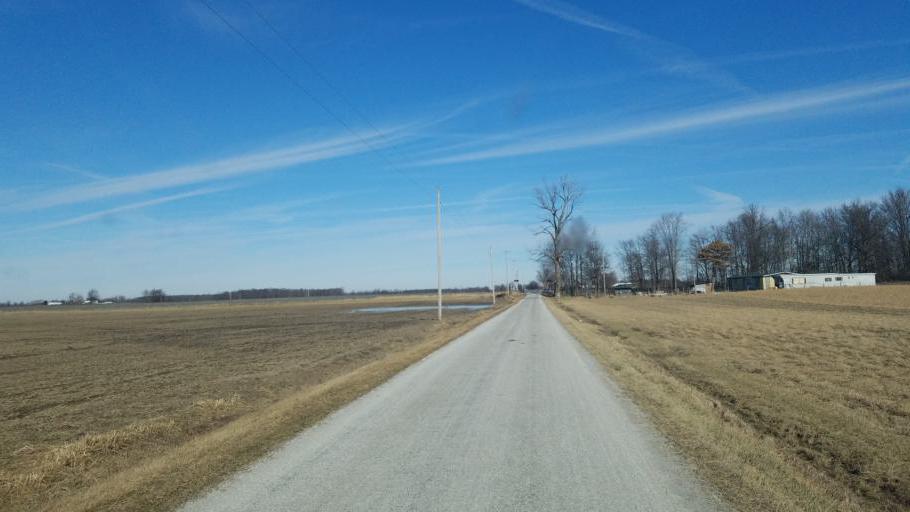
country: US
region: Ohio
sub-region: Union County
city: Richwood
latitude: 40.5646
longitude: -83.4183
